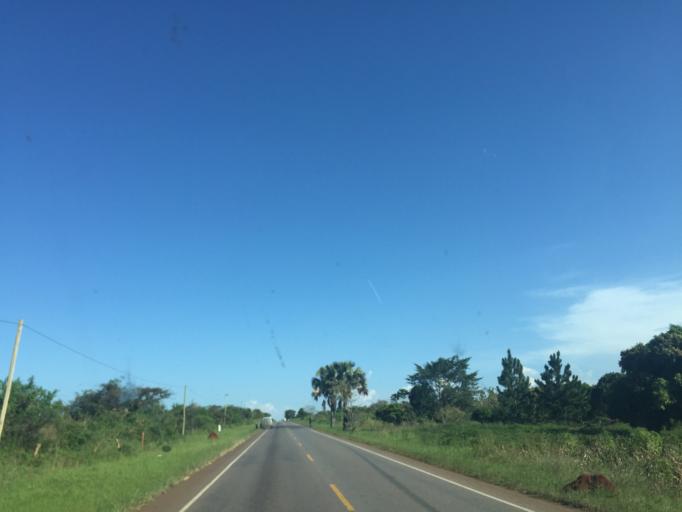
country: UG
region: Central Region
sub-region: Nakasongola District
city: Nakasongola
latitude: 1.3459
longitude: 32.3896
